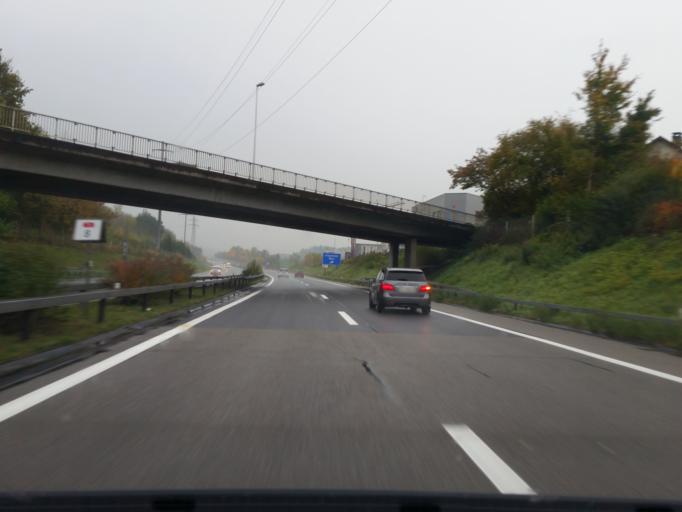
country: CH
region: Thurgau
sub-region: Frauenfeld District
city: Frauenfeld
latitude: 47.5635
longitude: 8.8773
